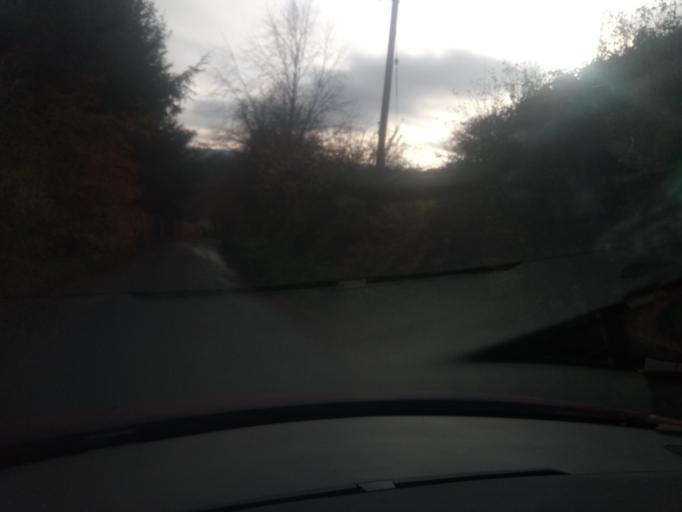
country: GB
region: Scotland
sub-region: The Scottish Borders
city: Jedburgh
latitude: 55.4788
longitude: -2.5613
